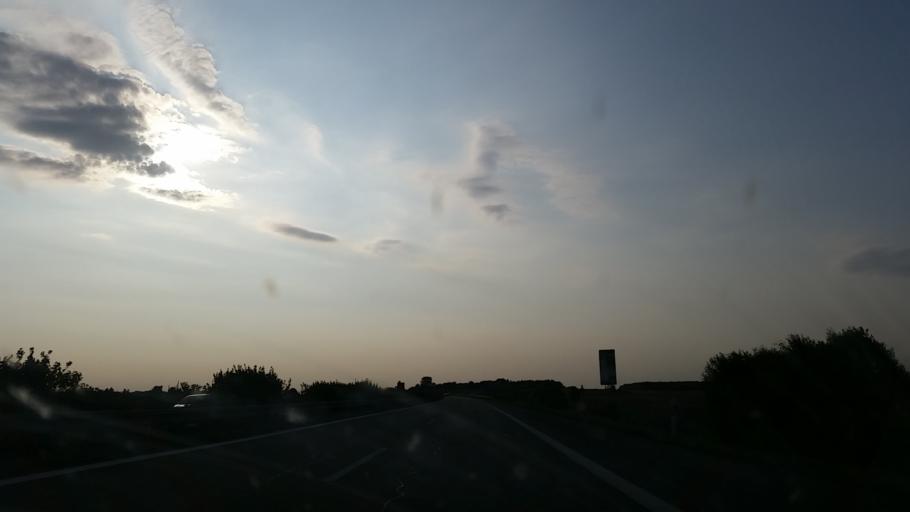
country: DE
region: Mecklenburg-Vorpommern
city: Grimmen
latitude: 54.0888
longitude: 13.1174
